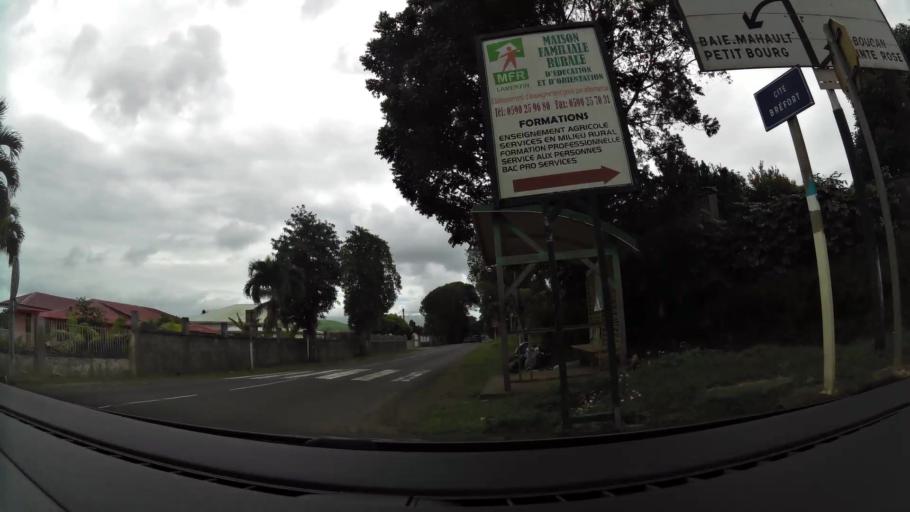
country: GP
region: Guadeloupe
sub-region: Guadeloupe
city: Lamentin
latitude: 16.2669
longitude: -61.6407
